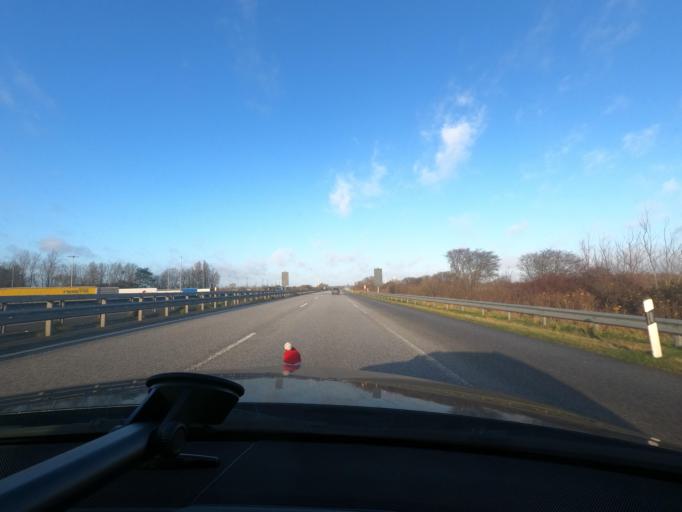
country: DE
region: Schleswig-Holstein
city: Bollingstedt
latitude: 54.6166
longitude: 9.4435
